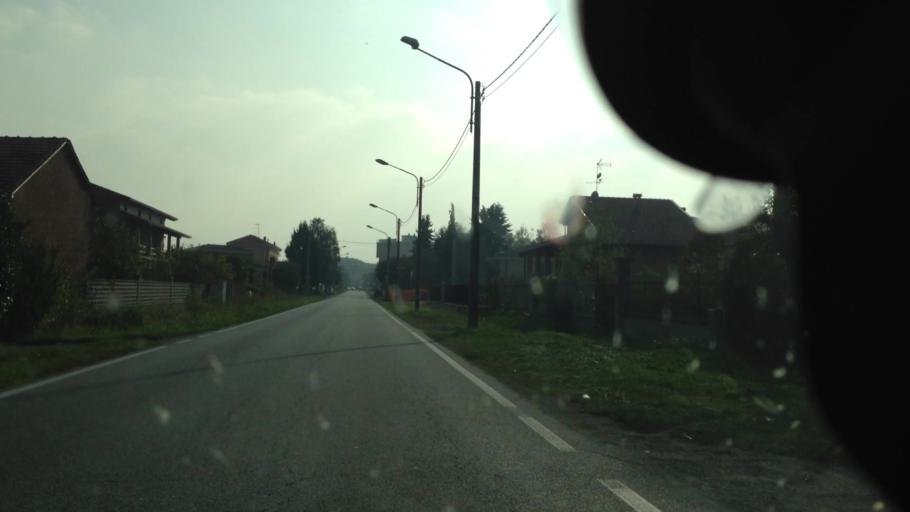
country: IT
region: Piedmont
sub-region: Provincia di Vercelli
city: Cigliano
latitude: 45.3153
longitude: 8.0281
